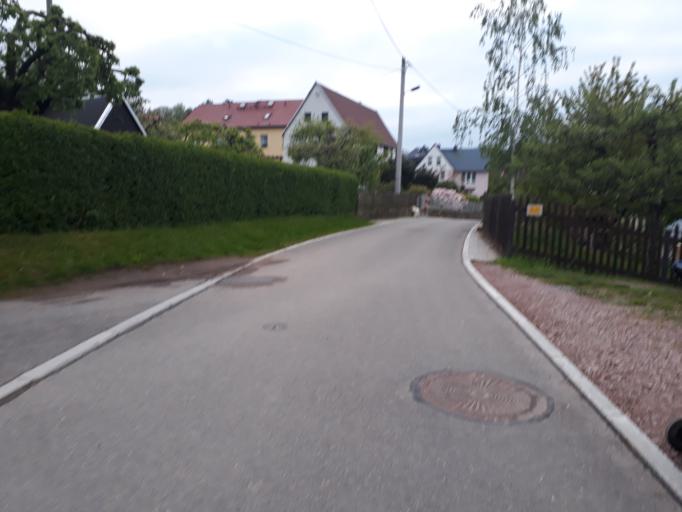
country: DE
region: Saxony
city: Reinhardtsgrimma
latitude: 50.8910
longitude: 13.7517
